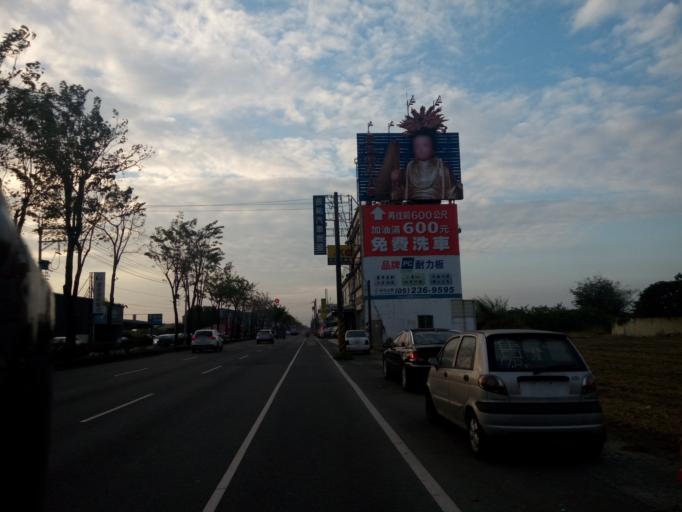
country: TW
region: Taiwan
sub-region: Chiayi
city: Jiayi Shi
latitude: 23.4879
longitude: 120.4117
